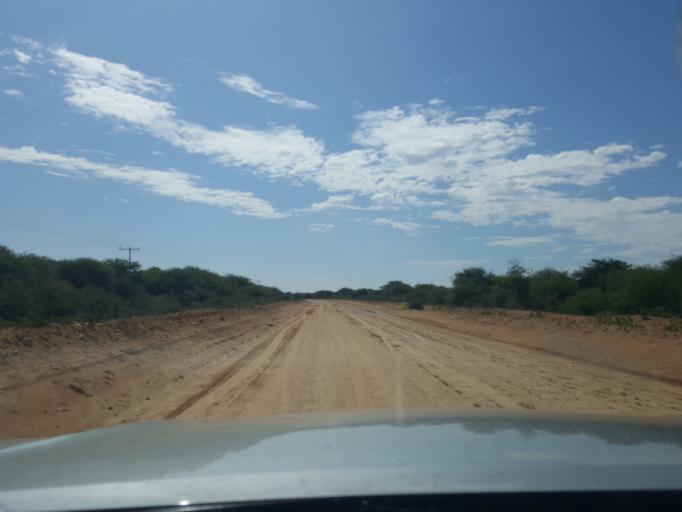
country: BW
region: Kweneng
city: Khudumelapye
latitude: -23.8900
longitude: 24.9192
